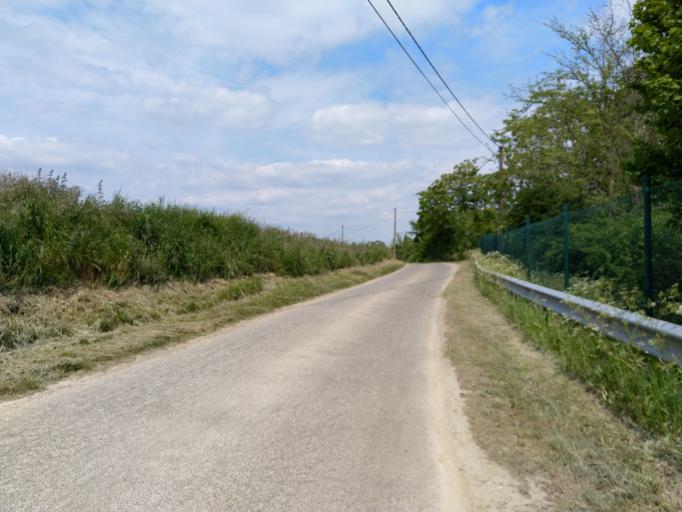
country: BE
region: Wallonia
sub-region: Province du Hainaut
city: Lens
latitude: 50.5640
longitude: 3.9195
